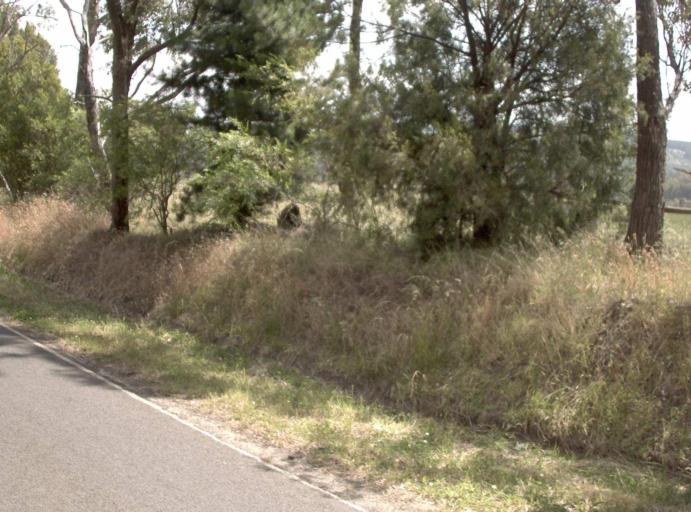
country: AU
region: Victoria
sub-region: Latrobe
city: Traralgon
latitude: -38.2937
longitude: 146.5387
